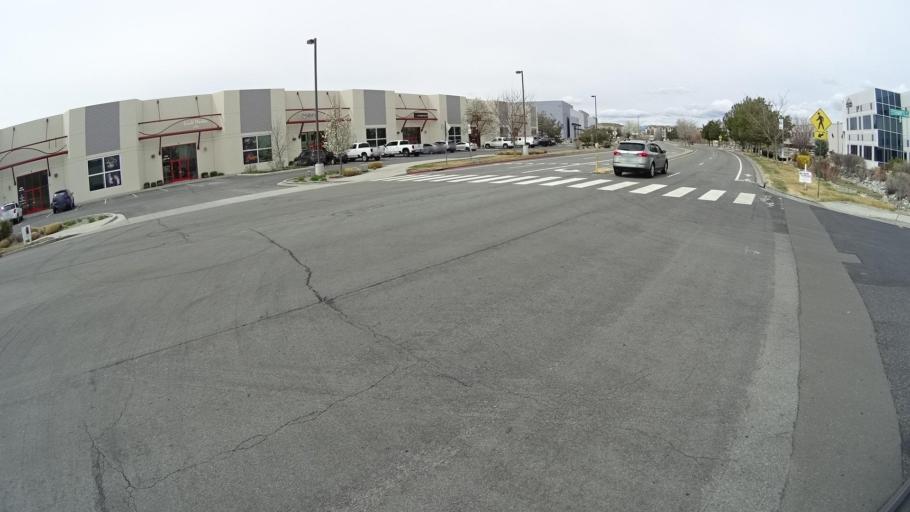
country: US
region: Nevada
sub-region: Washoe County
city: Sparks
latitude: 39.4503
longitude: -119.7504
